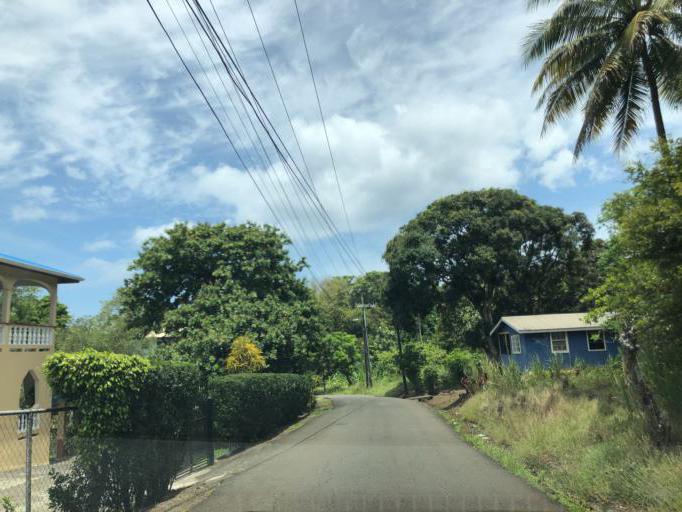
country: LC
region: Castries Quarter
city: Castries
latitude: 13.9937
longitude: -61.0097
